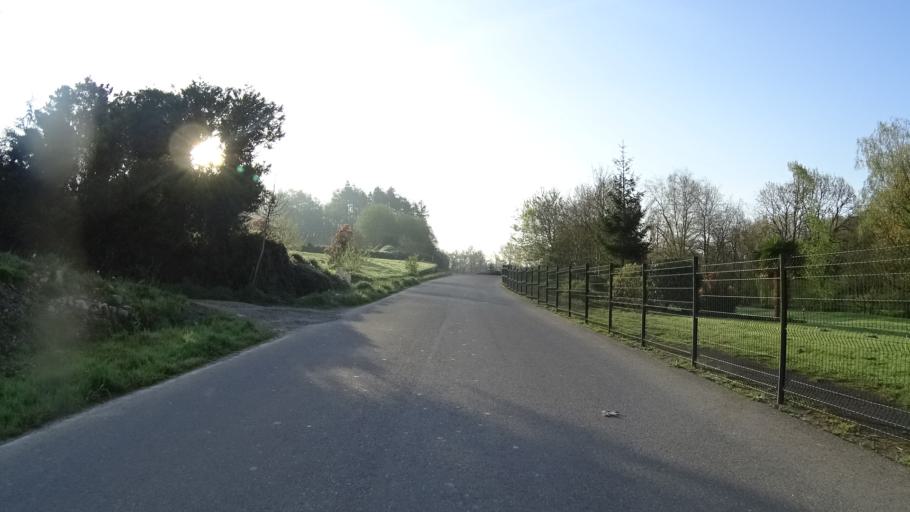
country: FR
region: Brittany
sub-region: Departement du Finistere
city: Sizun
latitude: 48.4113
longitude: -4.0828
